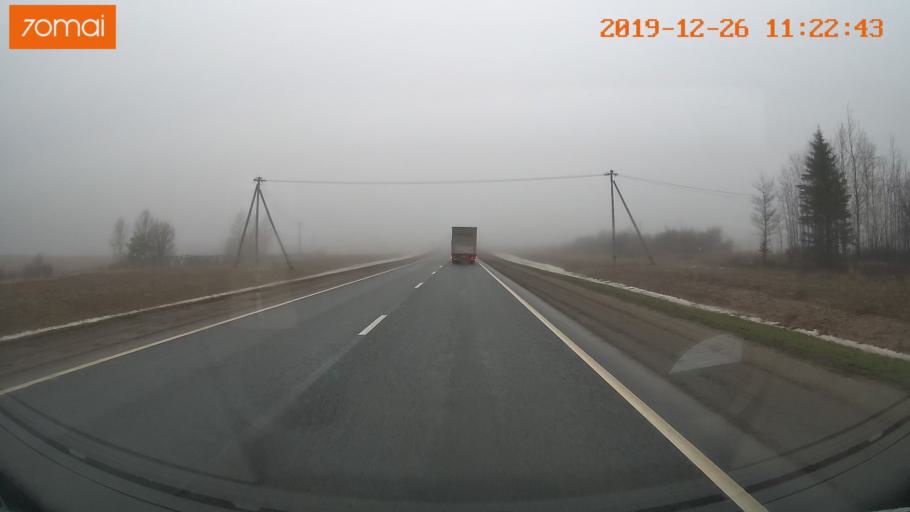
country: RU
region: Vologda
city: Chebsara
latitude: 59.1296
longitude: 38.9372
